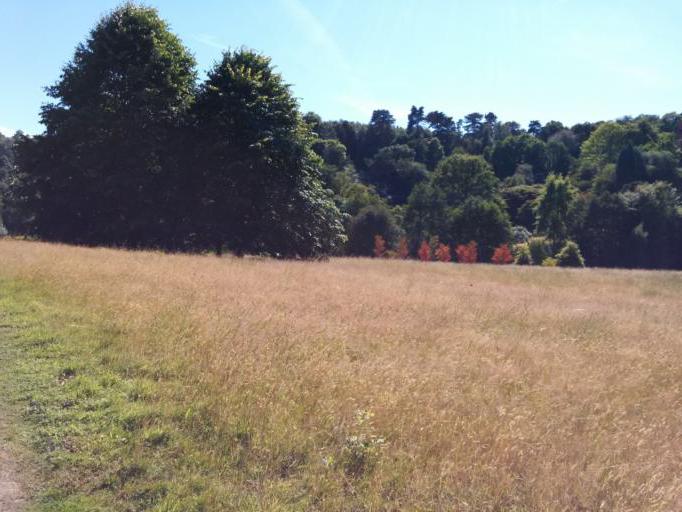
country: GB
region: England
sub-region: Surrey
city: Bramley
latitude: 51.1612
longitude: -0.5765
